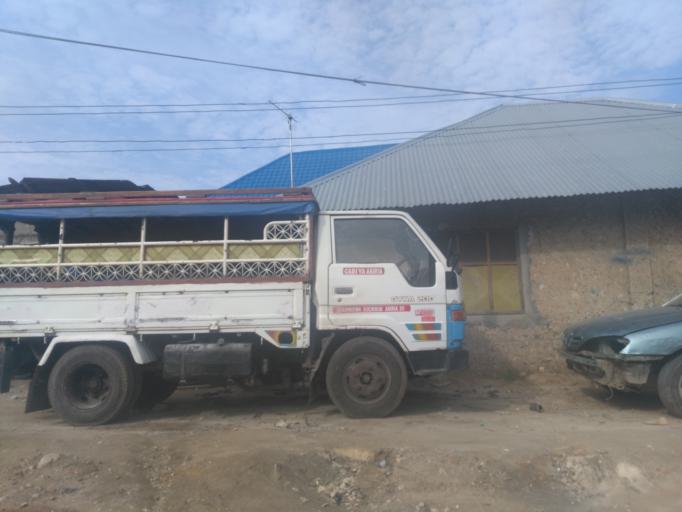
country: TZ
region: Zanzibar Urban/West
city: Zanzibar
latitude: -6.1614
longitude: 39.2097
